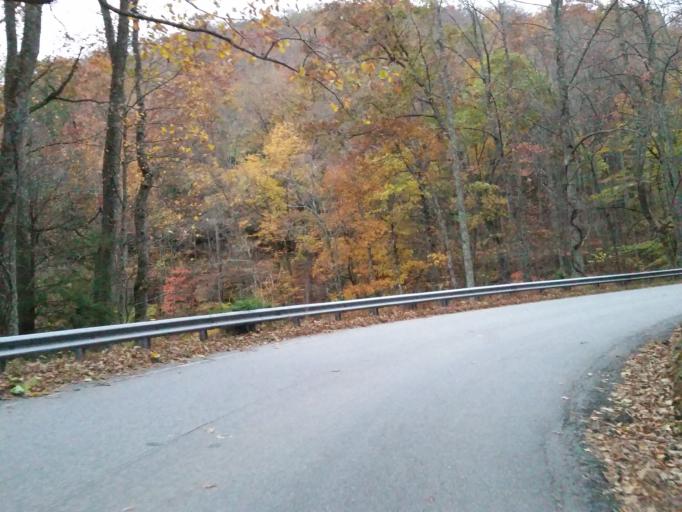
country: US
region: Georgia
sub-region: Lumpkin County
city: Dahlonega
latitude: 34.7018
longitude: -84.0394
